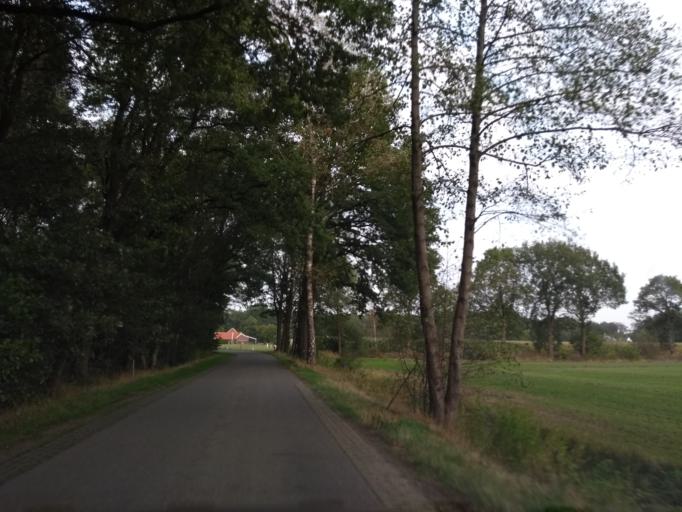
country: NL
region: Overijssel
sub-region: Gemeente Haaksbergen
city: Haaksbergen
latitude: 52.1189
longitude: 6.7466
